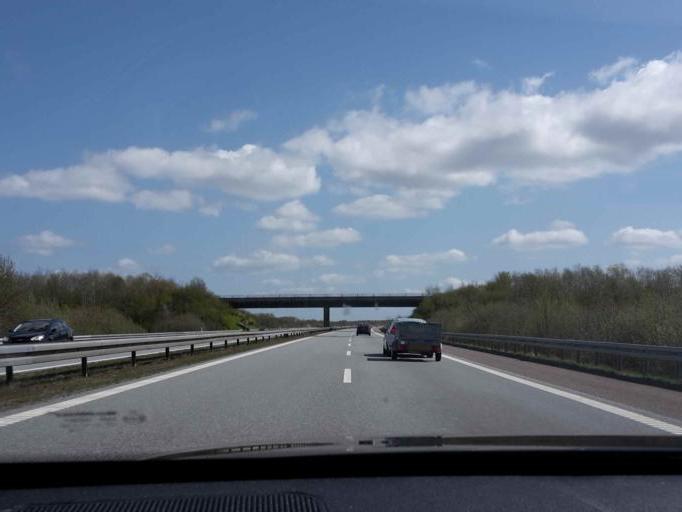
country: DK
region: South Denmark
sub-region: Vejen Kommune
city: Brorup
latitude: 55.5023
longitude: 9.0529
